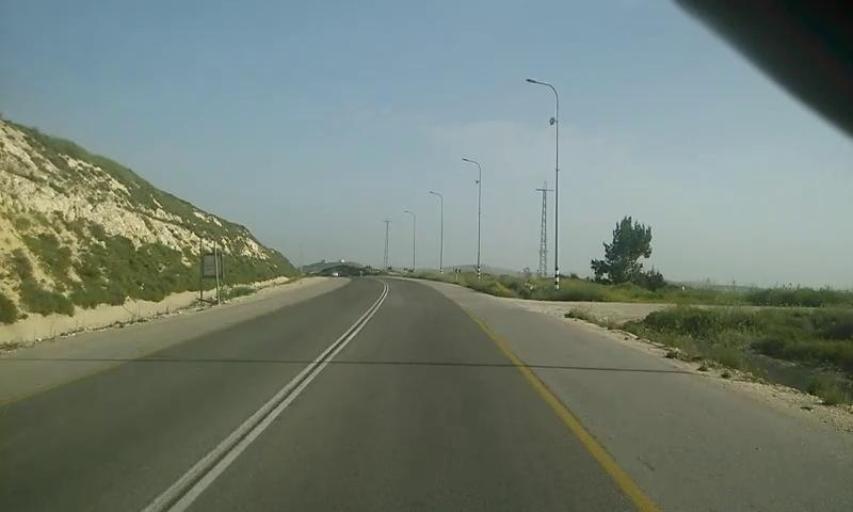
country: PS
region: West Bank
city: Sarrah
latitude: 32.1956
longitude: 35.1867
